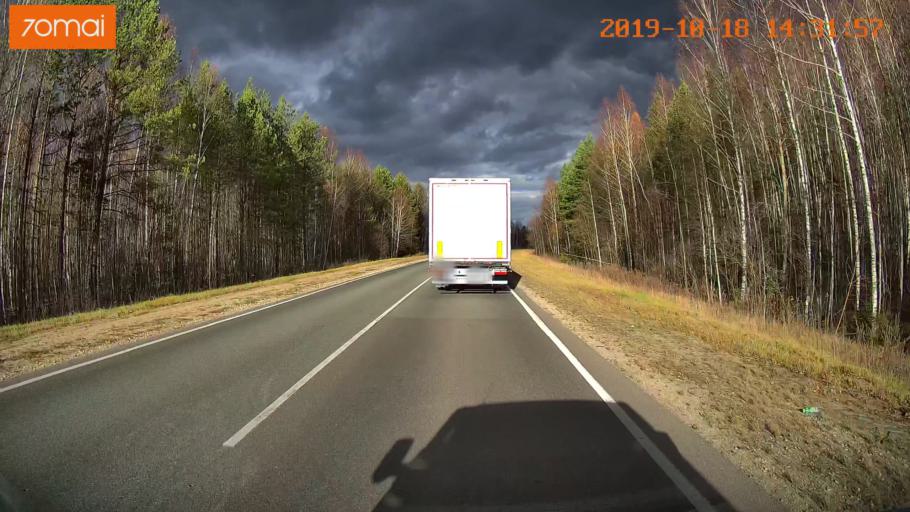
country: RU
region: Rjazan
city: Tuma
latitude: 55.1873
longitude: 40.5737
